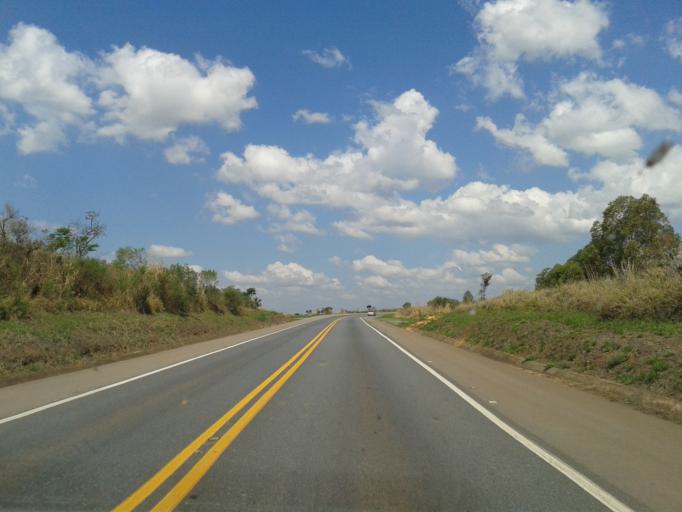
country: BR
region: Minas Gerais
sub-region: Campos Altos
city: Campos Altos
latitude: -19.6828
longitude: -46.0407
